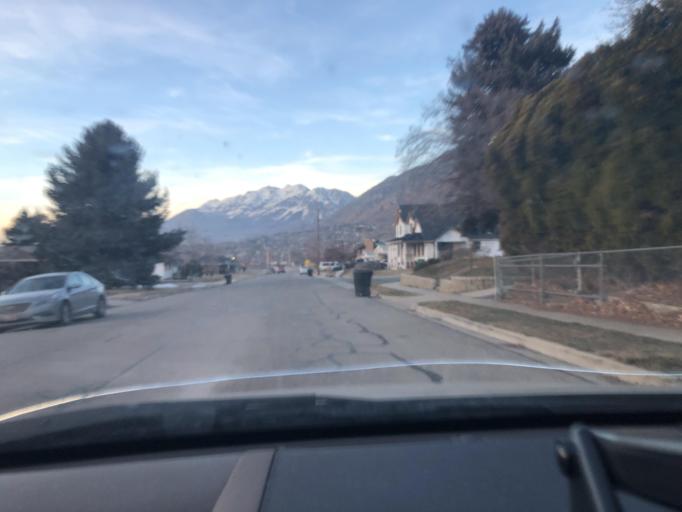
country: US
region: Utah
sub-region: Utah County
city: Provo
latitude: 40.2277
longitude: -111.6352
